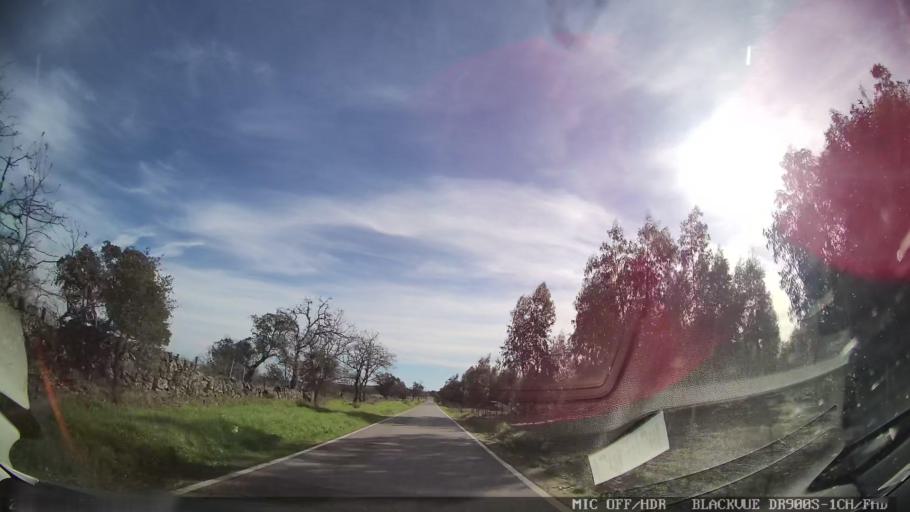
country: PT
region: Portalegre
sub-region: Nisa
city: Nisa
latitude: 39.4915
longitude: -7.7434
